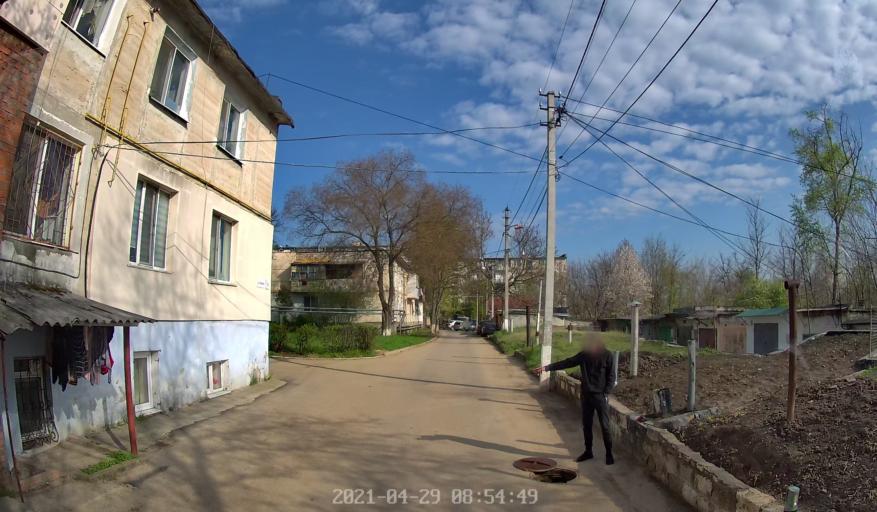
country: MD
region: Chisinau
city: Cricova
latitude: 47.1363
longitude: 28.8601
